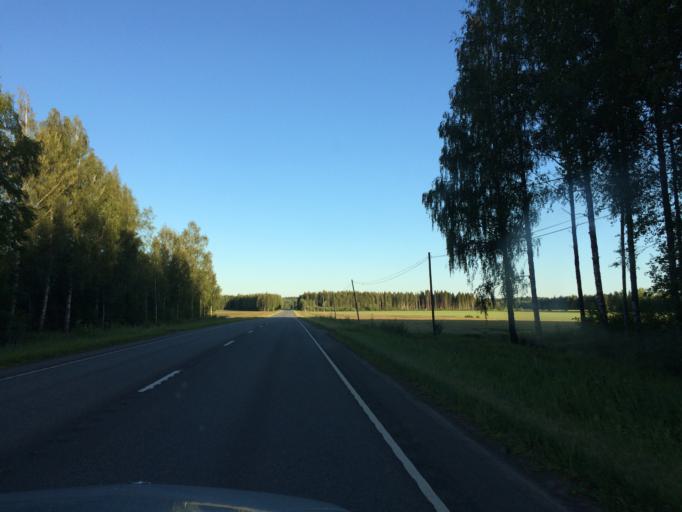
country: FI
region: Haeme
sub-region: Haemeenlinna
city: Tervakoski
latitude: 60.7834
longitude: 24.6859
